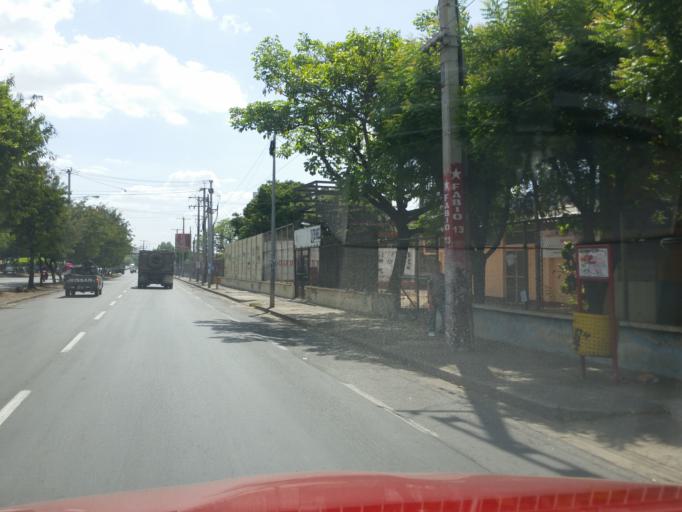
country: NI
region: Managua
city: Managua
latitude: 12.1536
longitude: -86.2567
